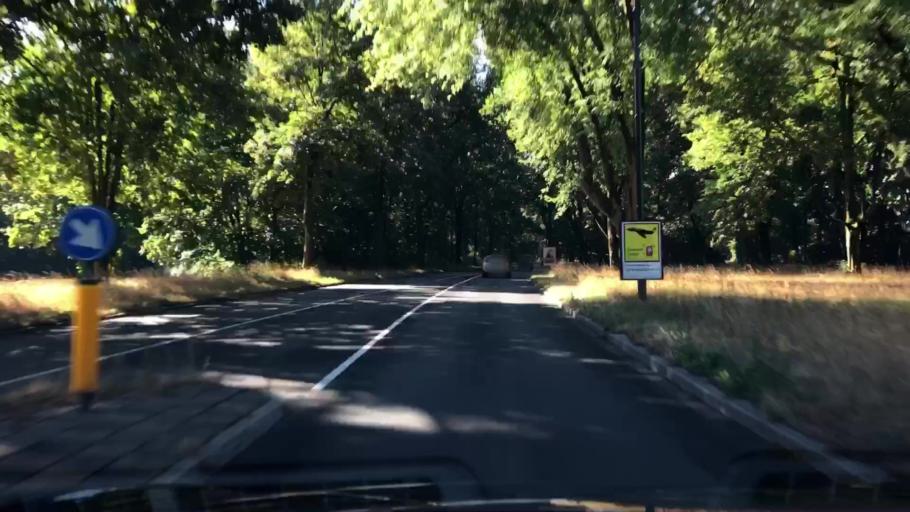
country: NL
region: Gelderland
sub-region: Gemeente Apeldoorn
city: Beekbergen
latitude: 52.1855
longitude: 5.9527
